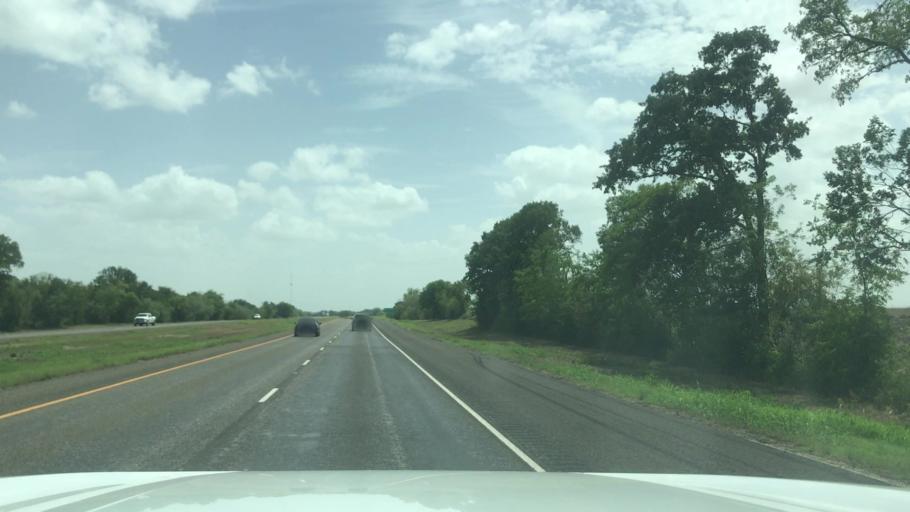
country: US
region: Texas
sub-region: Falls County
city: Marlin
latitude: 31.2901
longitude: -96.8752
